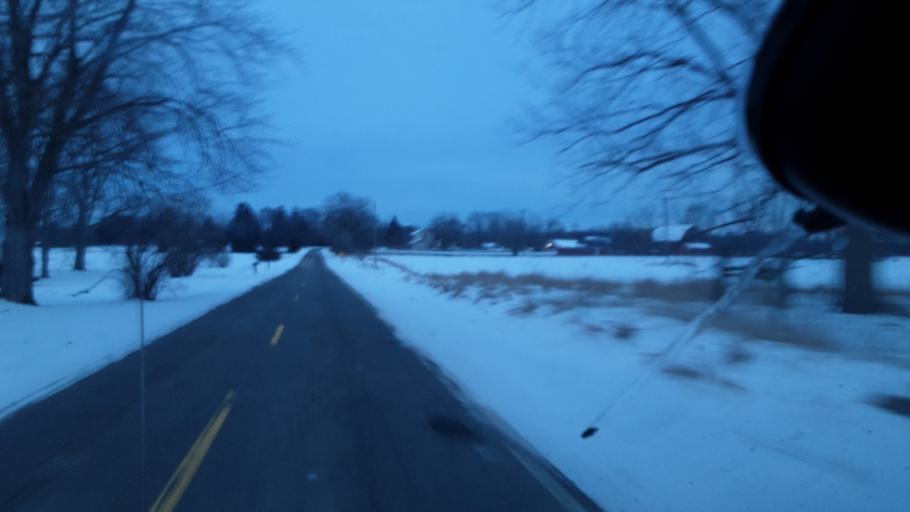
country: US
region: Michigan
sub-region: Ingham County
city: Stockbridge
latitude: 42.4081
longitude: -84.2852
